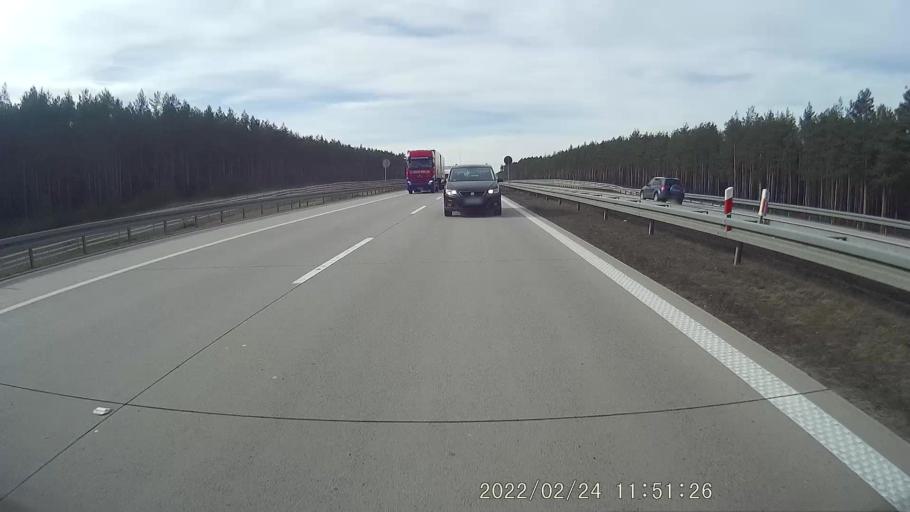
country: PL
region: Lower Silesian Voivodeship
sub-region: Powiat polkowicki
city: Radwanice
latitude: 51.6109
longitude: 15.9690
